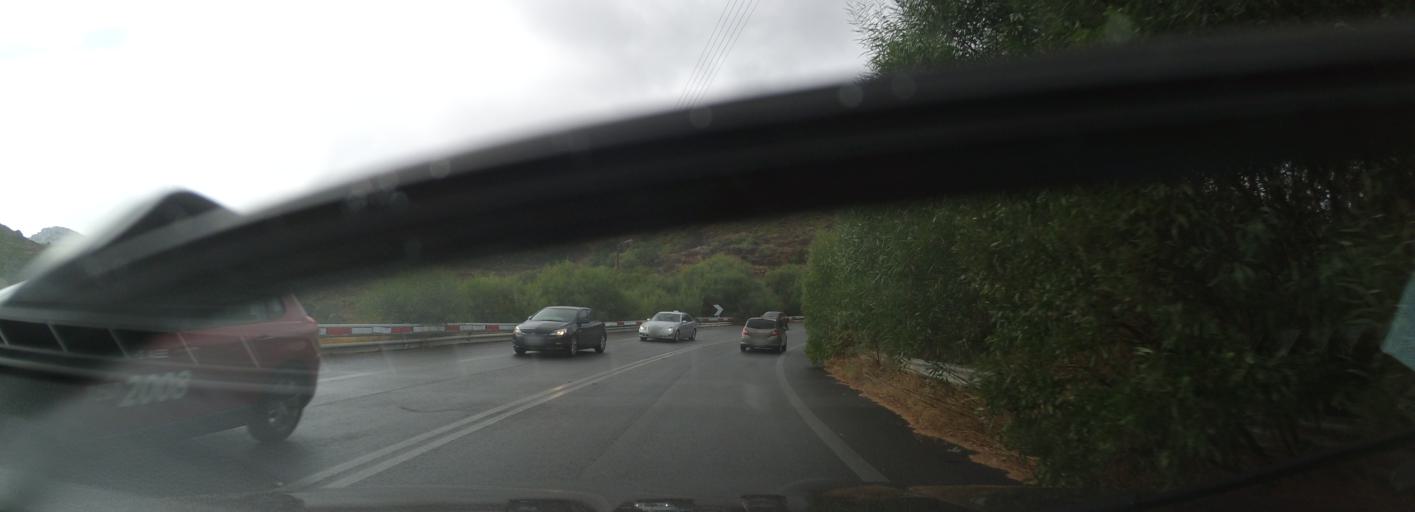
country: GR
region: Crete
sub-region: Nomos Irakleiou
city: Gazi
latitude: 35.3917
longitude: 25.0240
